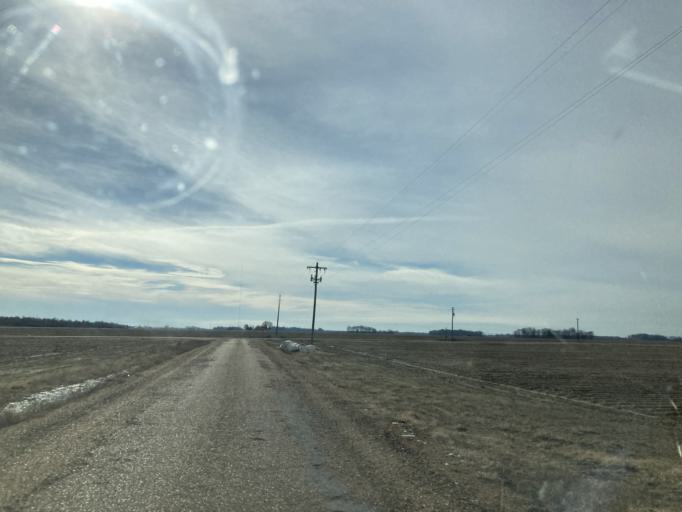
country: US
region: Mississippi
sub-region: Humphreys County
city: Belzoni
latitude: 33.0627
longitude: -90.6333
